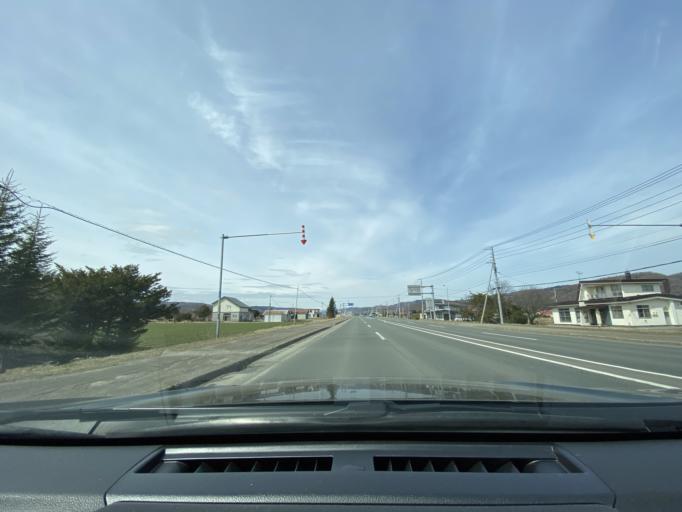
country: JP
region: Hokkaido
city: Kitami
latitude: 43.7951
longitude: 143.7361
